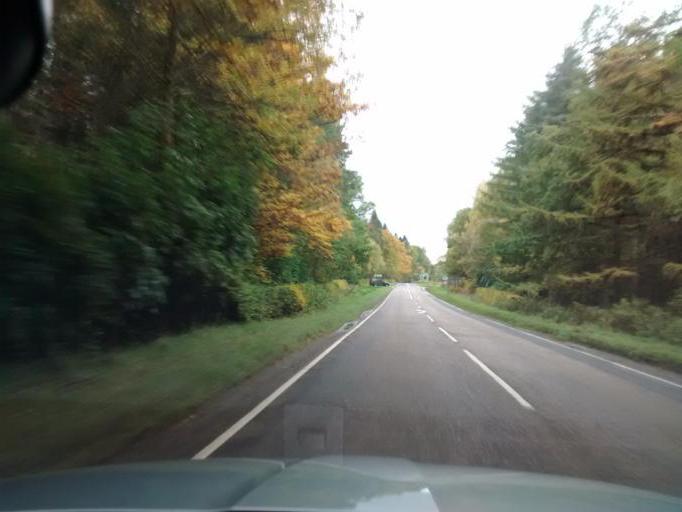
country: GB
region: Scotland
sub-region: Perth and Kinross
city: Blairgowrie
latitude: 56.5413
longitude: -3.3586
